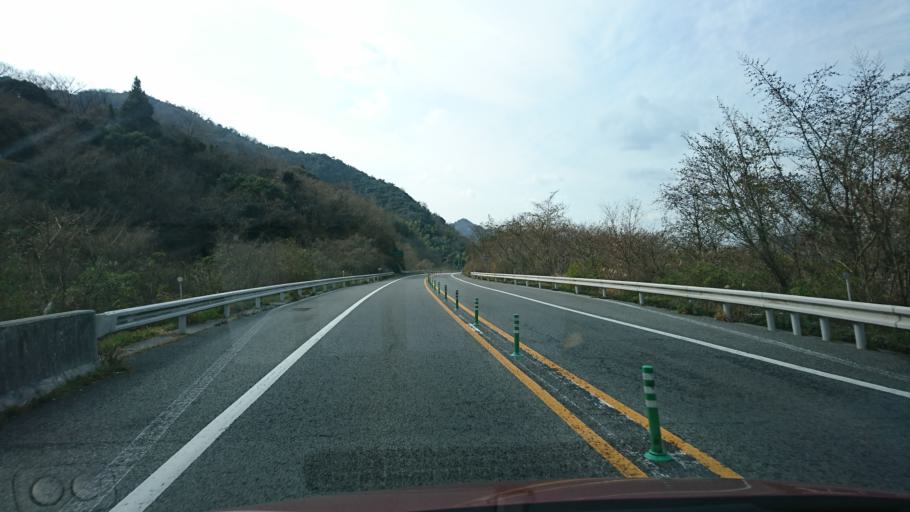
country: JP
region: Hiroshima
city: Innoshima
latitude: 34.1348
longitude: 133.0511
